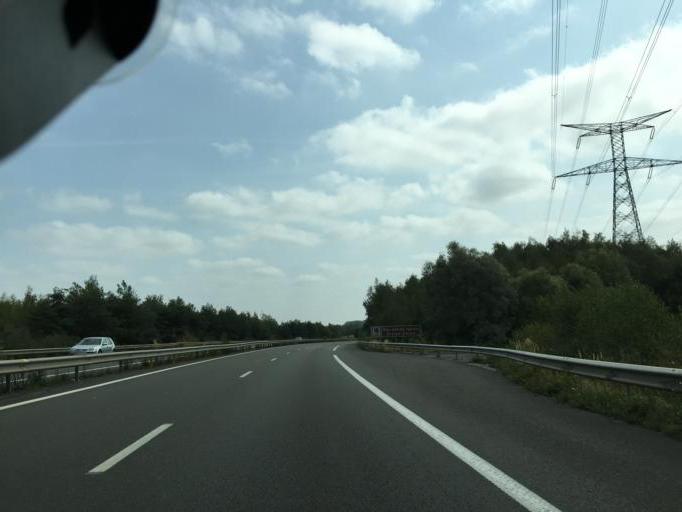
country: FR
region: Nord-Pas-de-Calais
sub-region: Departement du Nord
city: Vred
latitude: 50.3792
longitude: 3.2344
